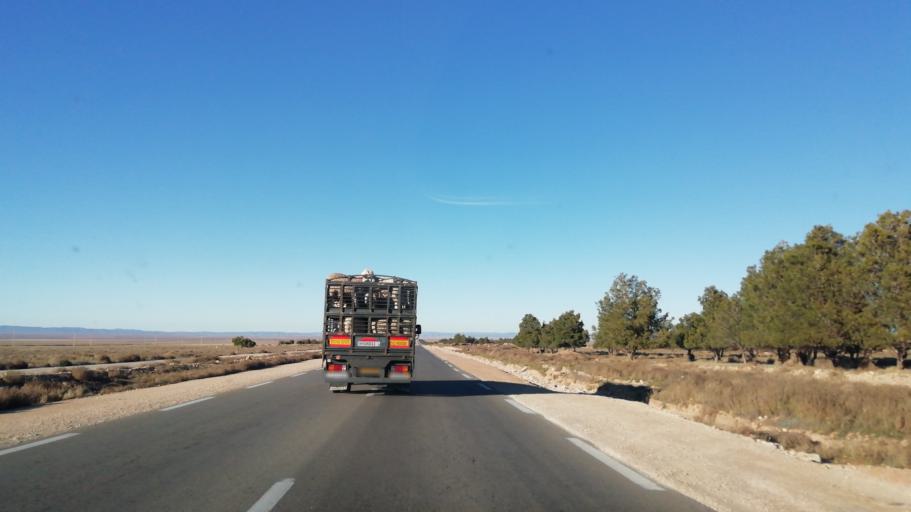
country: DZ
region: Tlemcen
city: Sebdou
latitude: 34.3141
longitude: -1.2625
